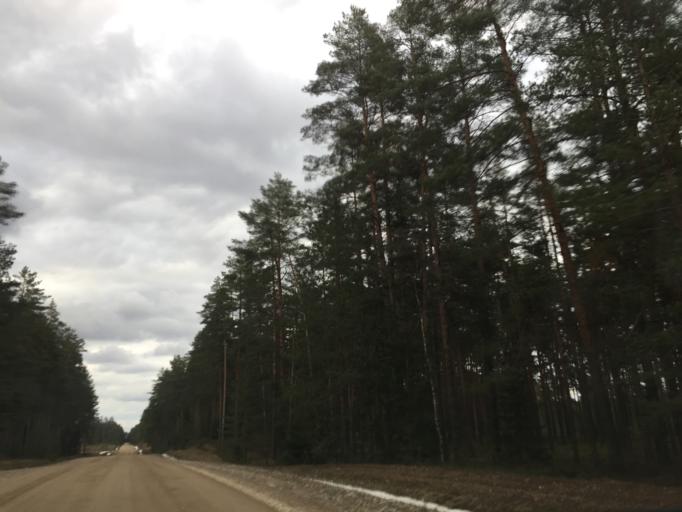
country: LV
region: Jaunjelgava
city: Jaunjelgava
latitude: 56.5827
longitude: 25.0292
